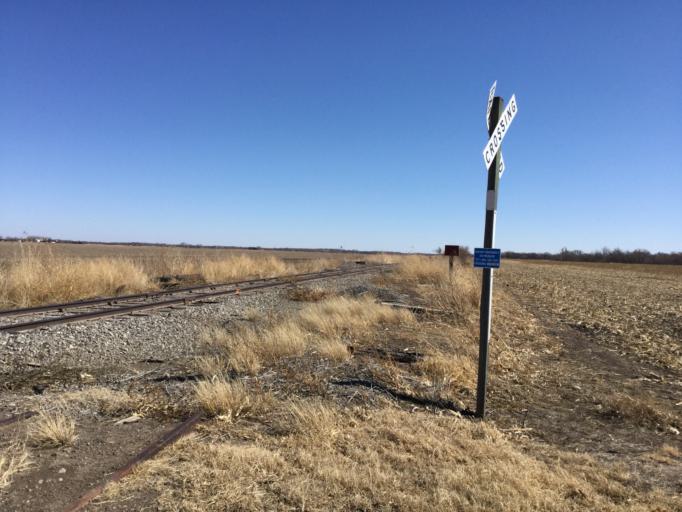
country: US
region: Kansas
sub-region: Pawnee County
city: Larned
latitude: 38.1662
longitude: -99.2141
